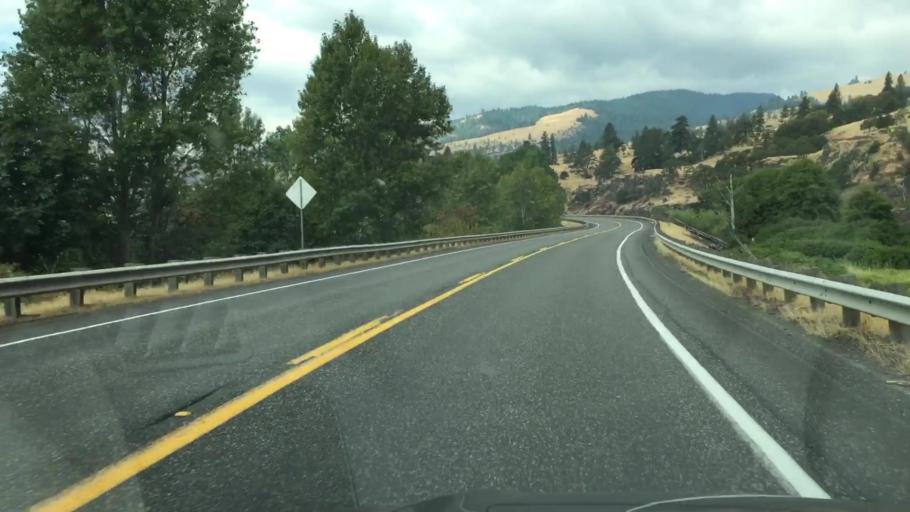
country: US
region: Oregon
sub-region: Wasco County
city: Chenoweth
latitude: 45.7097
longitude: -121.3406
